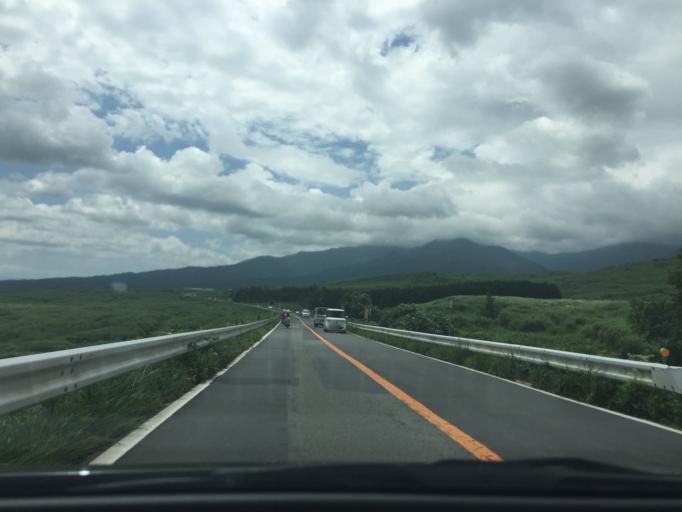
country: JP
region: Shizuoka
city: Gotemba
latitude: 35.2727
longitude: 138.8726
